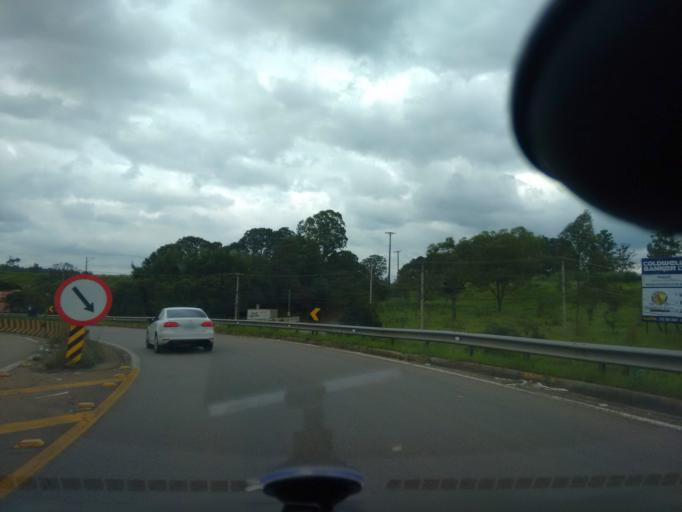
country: BR
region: Sao Paulo
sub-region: Indaiatuba
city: Indaiatuba
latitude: -23.0876
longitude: -47.1784
